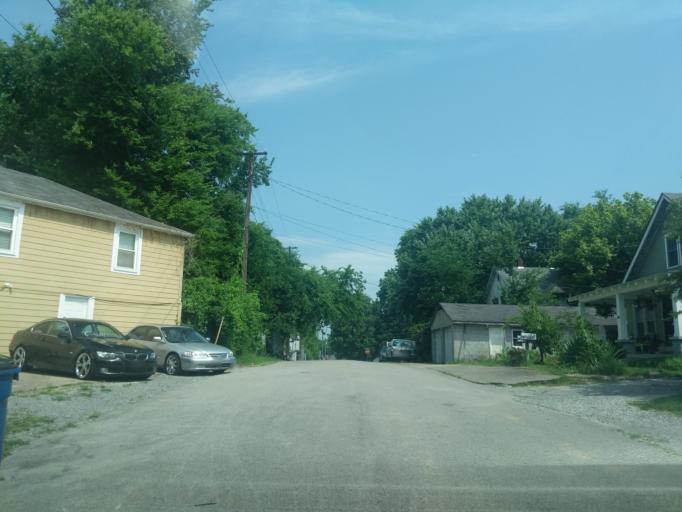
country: US
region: Tennessee
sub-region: Davidson County
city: Lakewood
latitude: 36.2691
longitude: -86.6647
